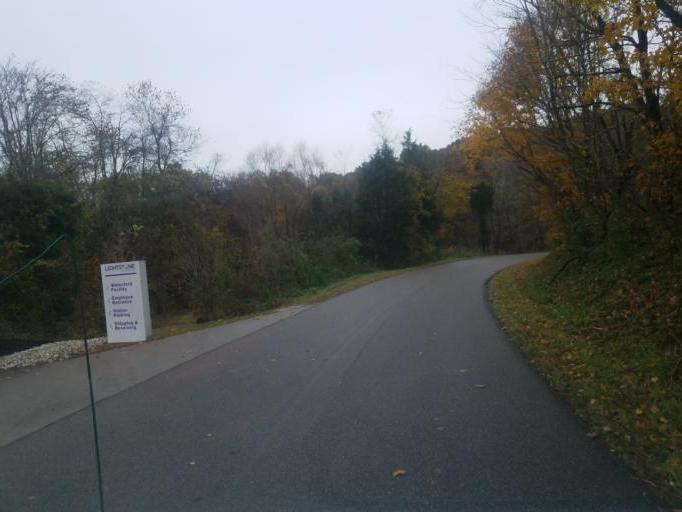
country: US
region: Ohio
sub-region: Washington County
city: Beverly
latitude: 39.5359
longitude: -81.7157
